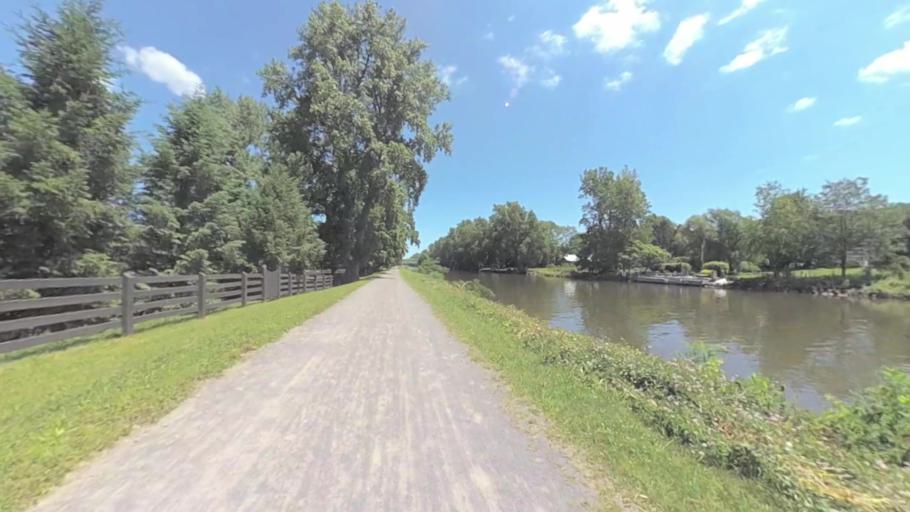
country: US
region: New York
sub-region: Monroe County
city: Fairport
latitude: 43.0703
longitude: -77.4675
